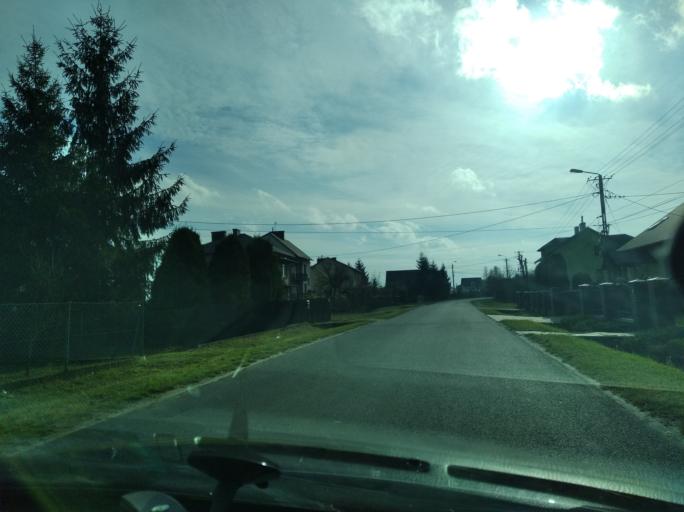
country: PL
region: Subcarpathian Voivodeship
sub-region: Powiat ropczycko-sedziszowski
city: Sedziszow Malopolski
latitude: 50.1095
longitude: 21.7348
